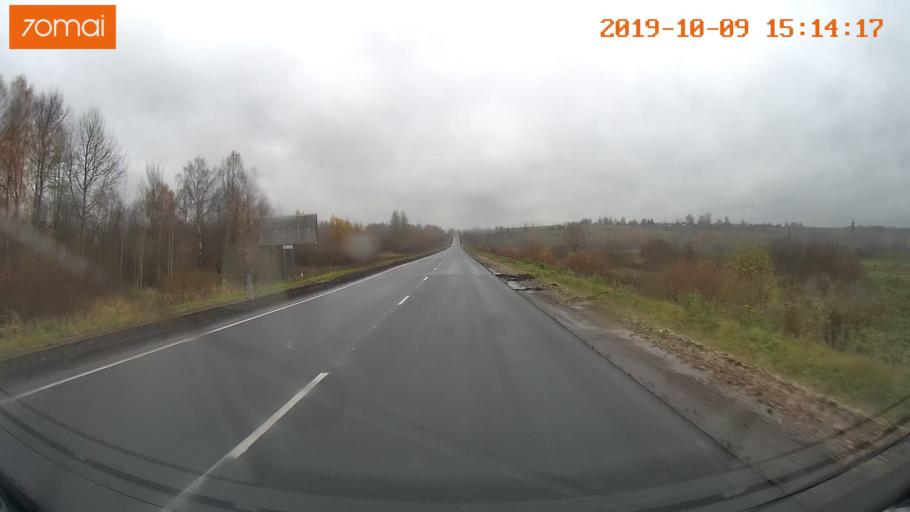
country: RU
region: Kostroma
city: Susanino
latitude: 58.1366
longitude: 41.6042
